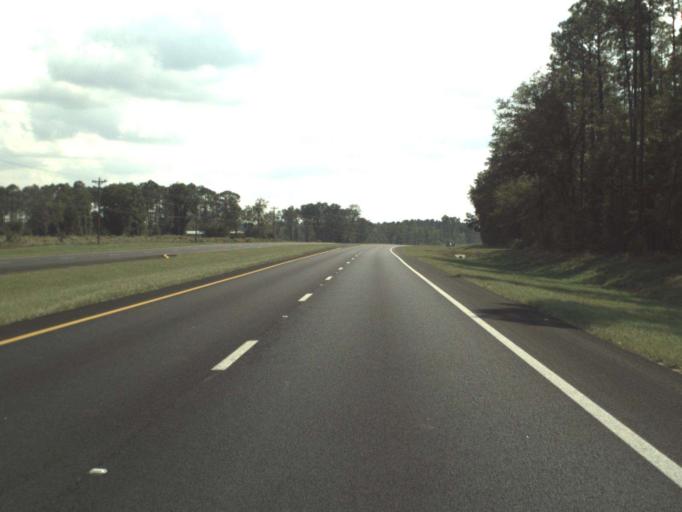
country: US
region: Florida
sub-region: Bay County
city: Laguna Beach
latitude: 30.4899
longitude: -85.8423
